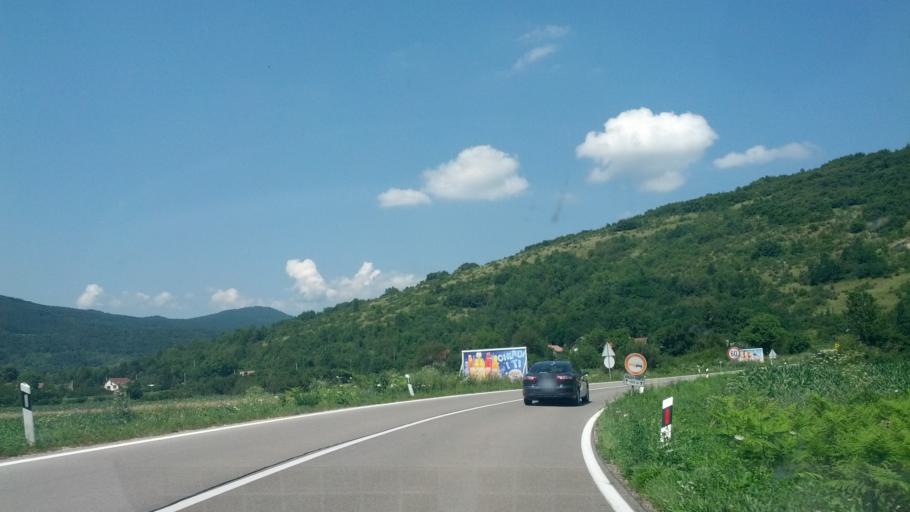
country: BA
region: Federation of Bosnia and Herzegovina
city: Izacic
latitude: 44.8797
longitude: 15.7274
